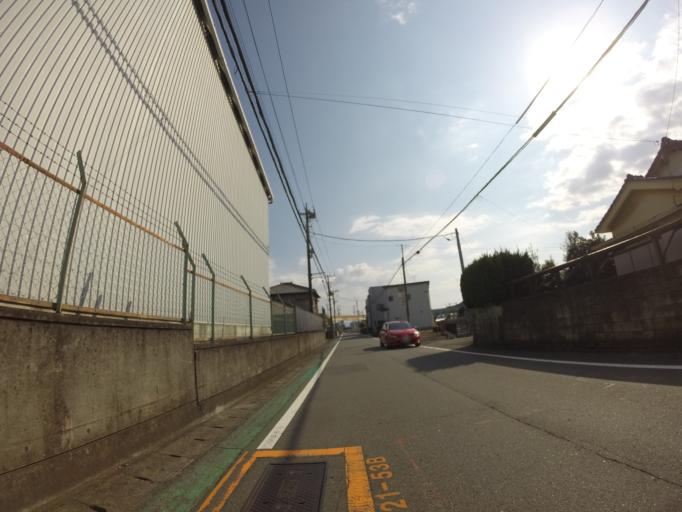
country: JP
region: Shizuoka
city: Fujinomiya
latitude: 35.2027
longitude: 138.6359
